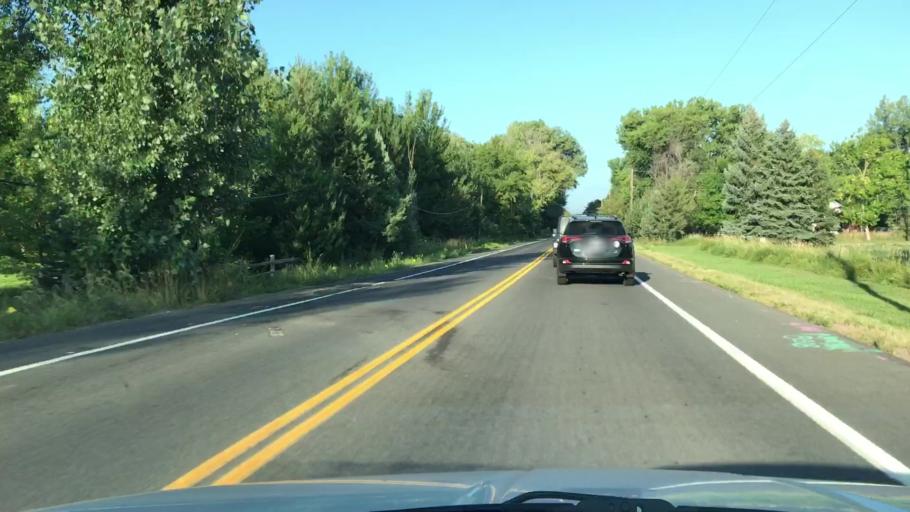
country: US
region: Colorado
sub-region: Boulder County
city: Gunbarrel
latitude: 40.0346
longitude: -105.1701
